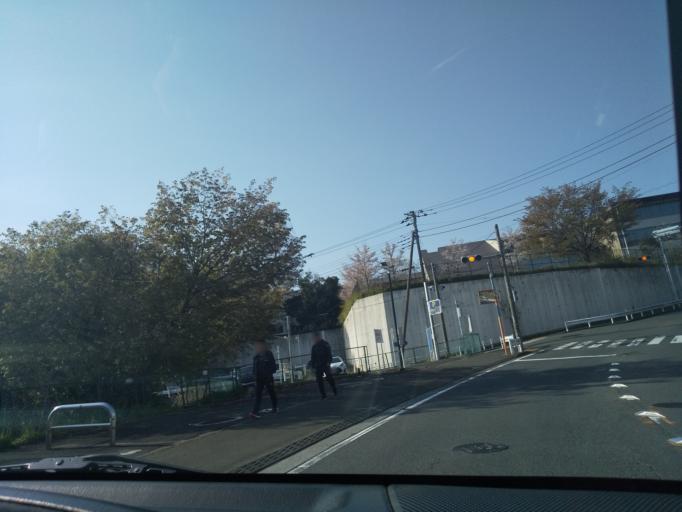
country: JP
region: Tokyo
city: Hino
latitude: 35.6450
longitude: 139.4191
